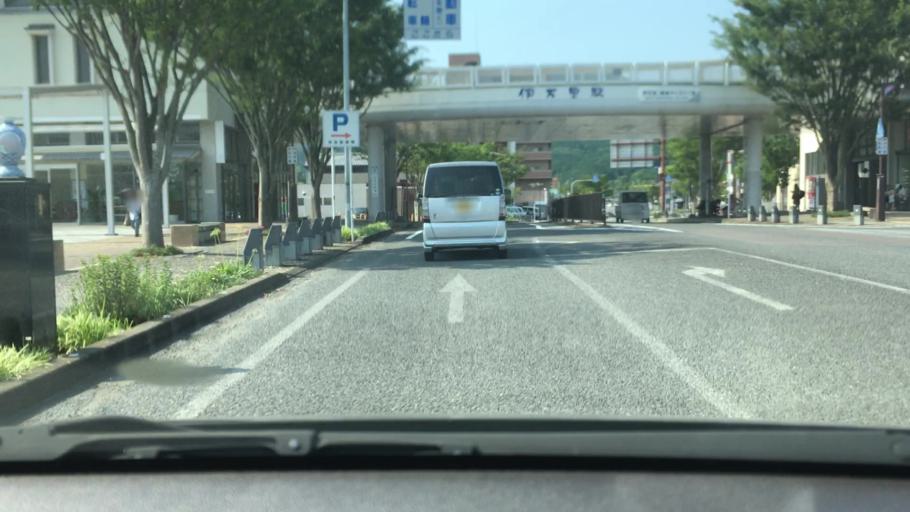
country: JP
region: Saga Prefecture
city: Imaricho-ko
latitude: 33.2723
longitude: 129.8767
